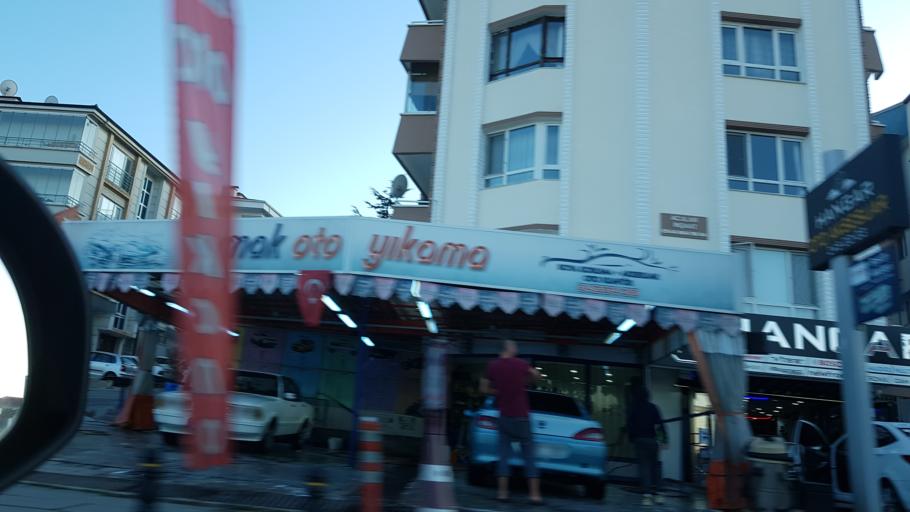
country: TR
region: Ankara
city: Etimesgut
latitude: 39.9467
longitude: 32.6721
